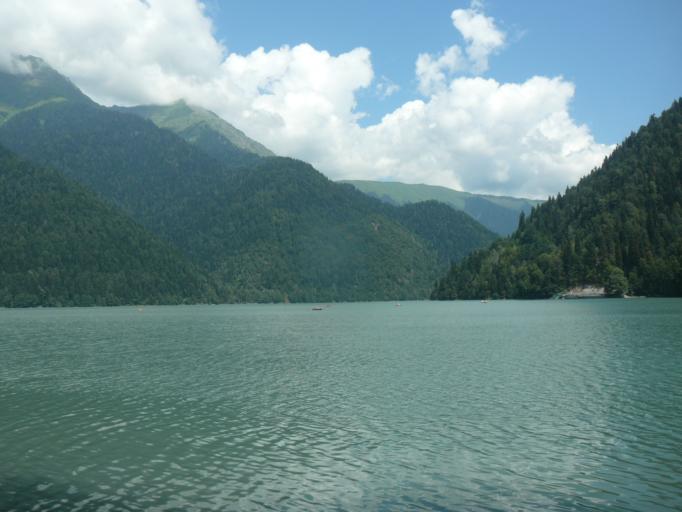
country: GE
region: Abkhazia
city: Gagra
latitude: 43.4740
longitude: 40.5317
